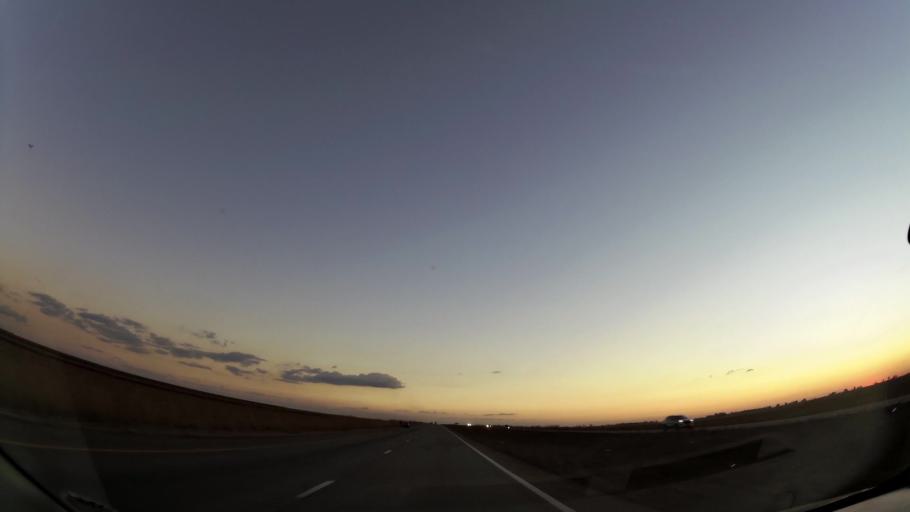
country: ZA
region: Mpumalanga
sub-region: Nkangala District Municipality
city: Witbank
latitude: -25.9805
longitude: 29.1668
